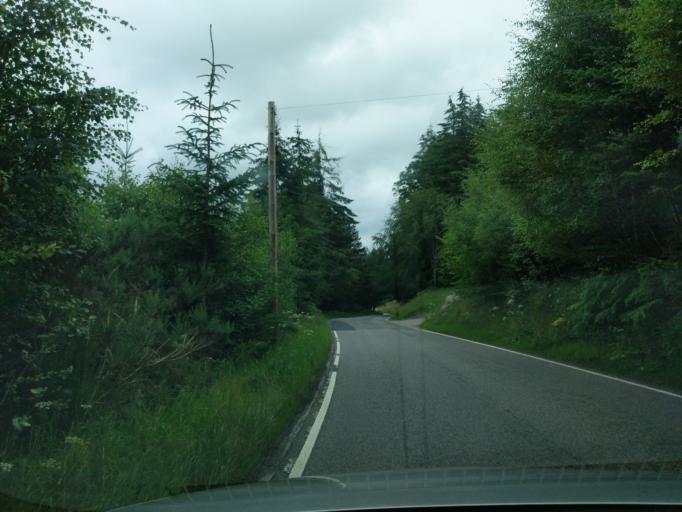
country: GB
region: Scotland
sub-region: Moray
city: Forres
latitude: 57.5212
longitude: -3.6756
